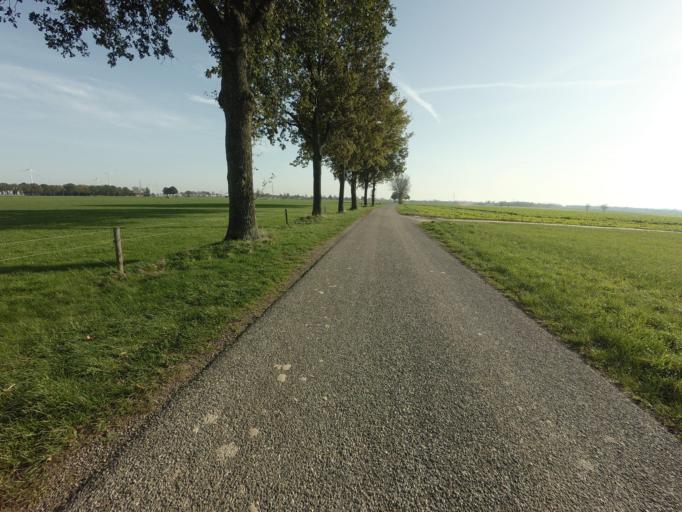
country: NL
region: Limburg
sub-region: Gemeente Echt-Susteren
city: Koningsbosch
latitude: 51.0447
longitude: 5.9419
